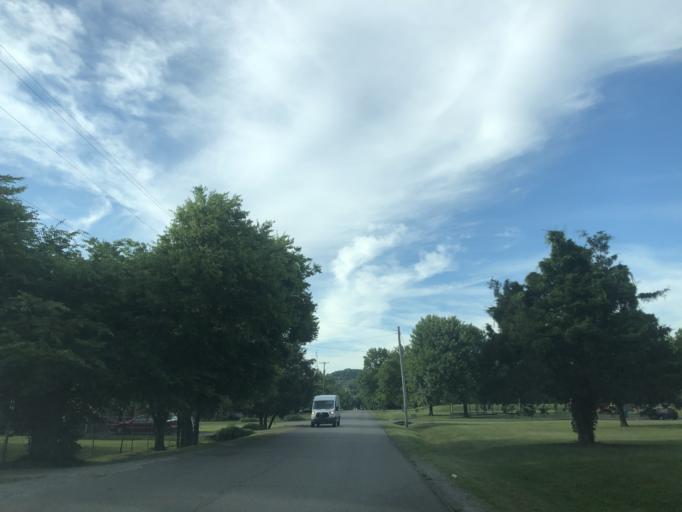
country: US
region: Tennessee
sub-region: Davidson County
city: Nashville
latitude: 36.2130
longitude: -86.8446
